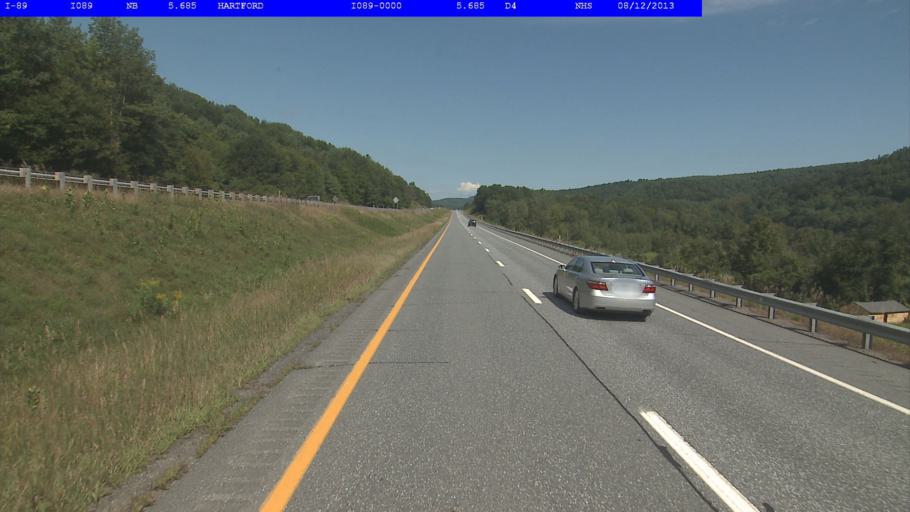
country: US
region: Vermont
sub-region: Windsor County
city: White River Junction
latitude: 43.6881
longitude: -72.4037
